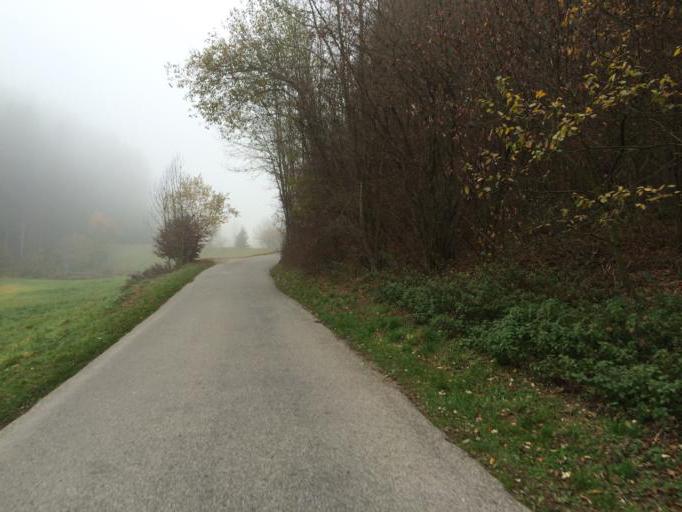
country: CH
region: Bern
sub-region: Bern-Mittelland District
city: Koniz
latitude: 46.9144
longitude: 7.4292
